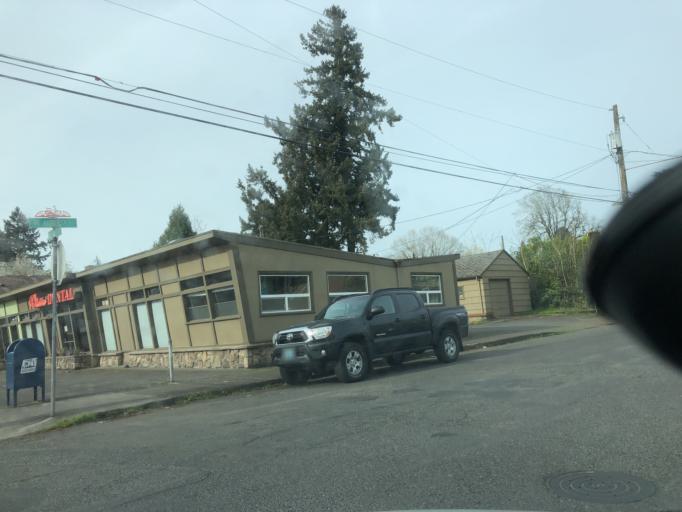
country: US
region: Oregon
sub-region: Multnomah County
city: Portland
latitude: 45.5583
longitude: -122.6205
